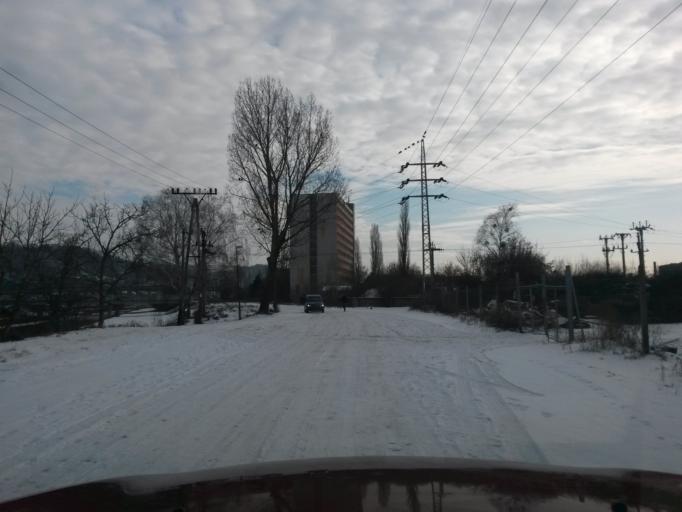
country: SK
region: Kosicky
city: Kosice
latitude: 48.7242
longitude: 21.2713
